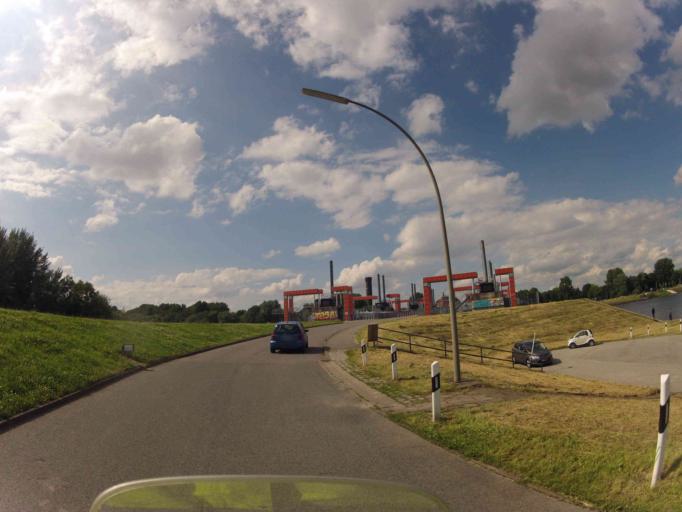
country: DE
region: Hamburg
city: Rothenburgsort
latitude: 53.5276
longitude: 10.0445
